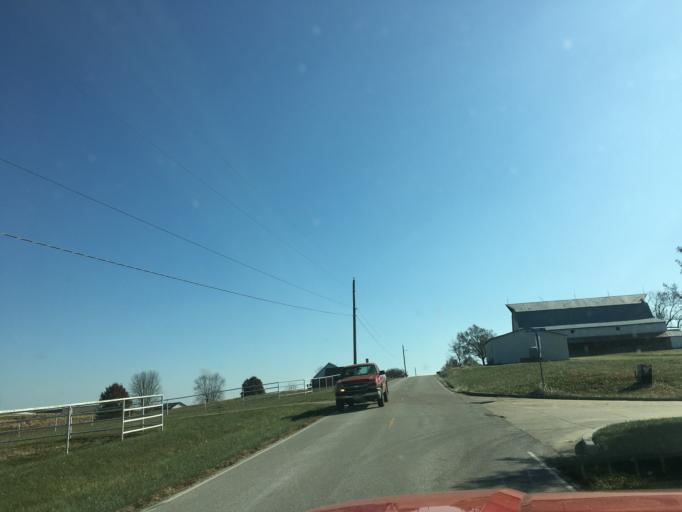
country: US
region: Missouri
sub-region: Cole County
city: Wardsville
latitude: 38.5000
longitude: -92.1836
